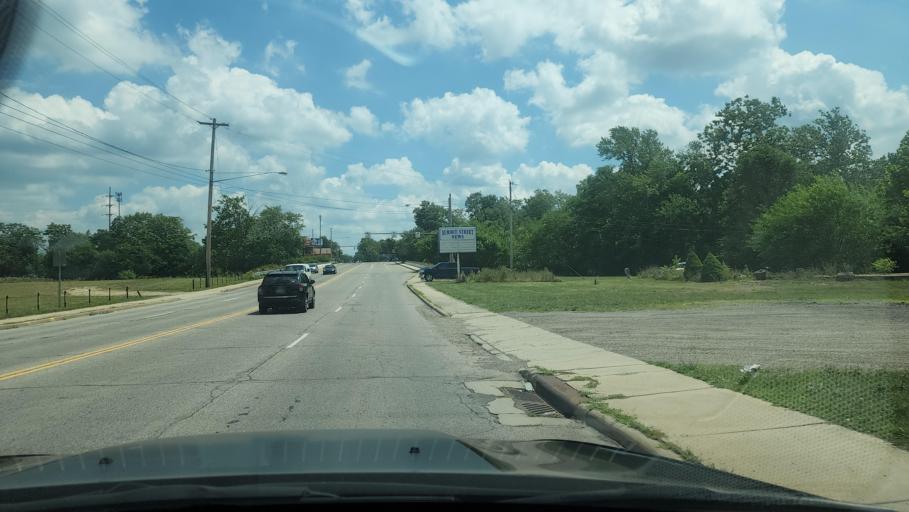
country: US
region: Ohio
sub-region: Trumbull County
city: Warren
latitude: 41.2430
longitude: -80.8290
